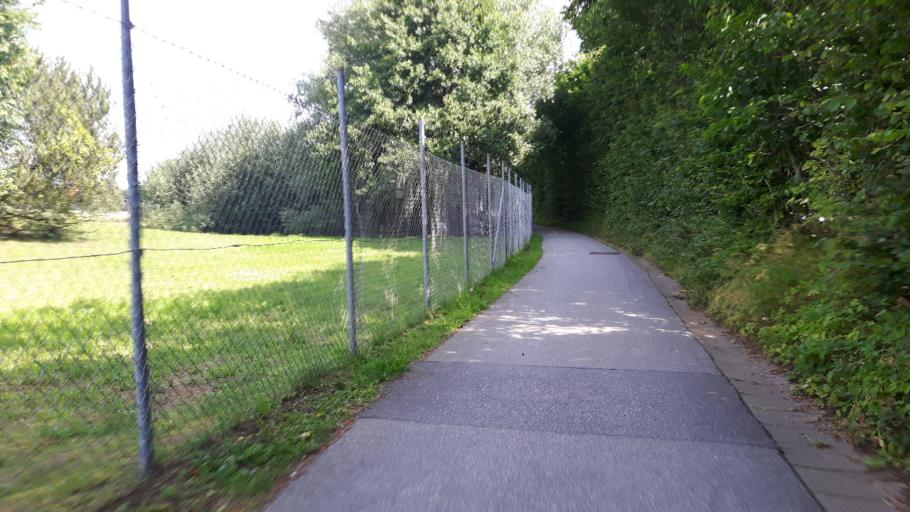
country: DE
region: Schleswig-Holstein
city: Travemuende
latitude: 53.9434
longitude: 10.8477
